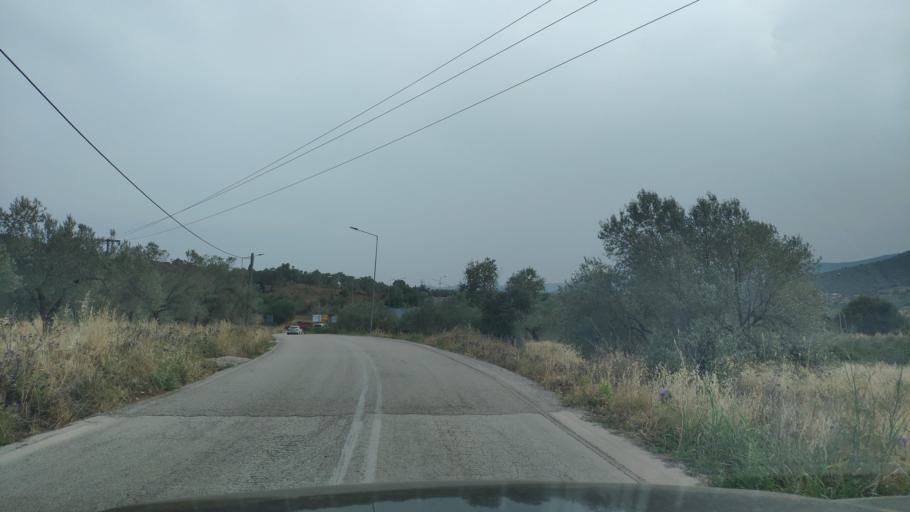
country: GR
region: Peloponnese
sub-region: Nomos Argolidos
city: Palaia Epidavros
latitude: 37.5720
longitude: 23.1493
